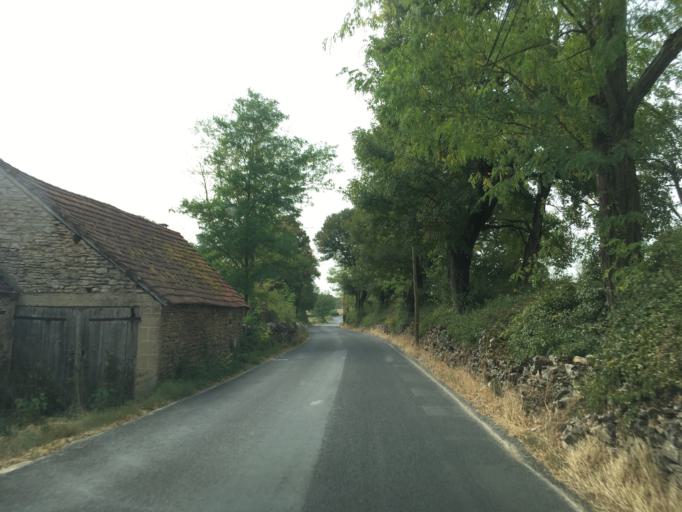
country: FR
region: Midi-Pyrenees
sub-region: Departement du Lot
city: Gramat
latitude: 44.8095
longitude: 1.6154
